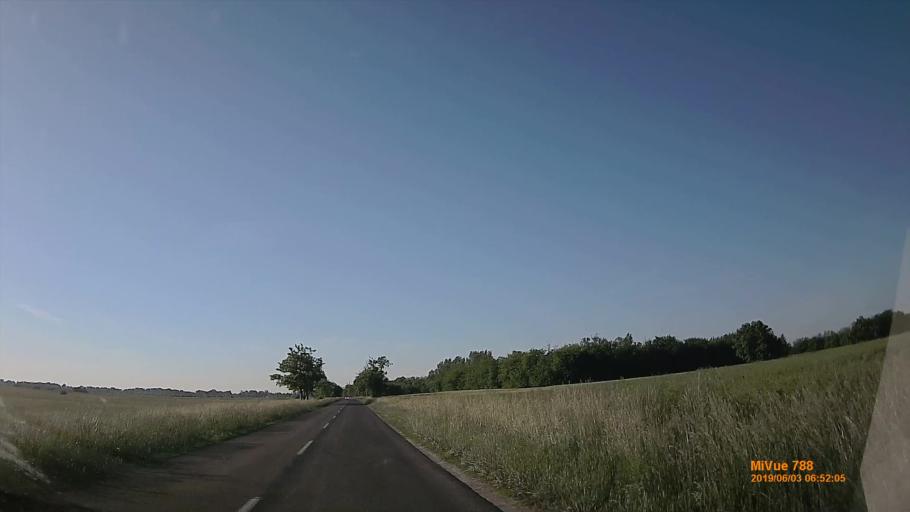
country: HU
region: Pest
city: Bugyi
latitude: 47.2048
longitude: 19.1926
